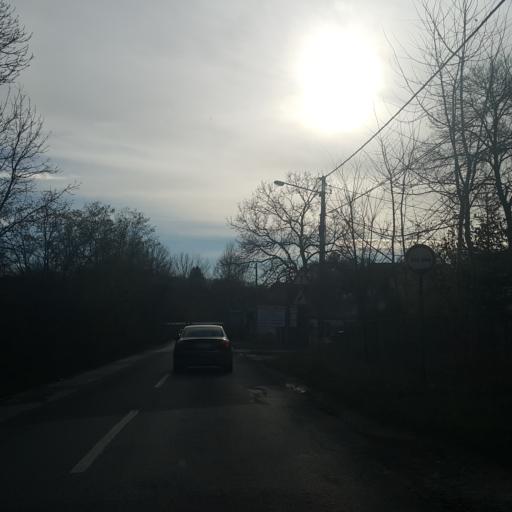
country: RS
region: Central Serbia
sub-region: Belgrade
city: Lazarevac
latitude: 44.4068
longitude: 20.2643
